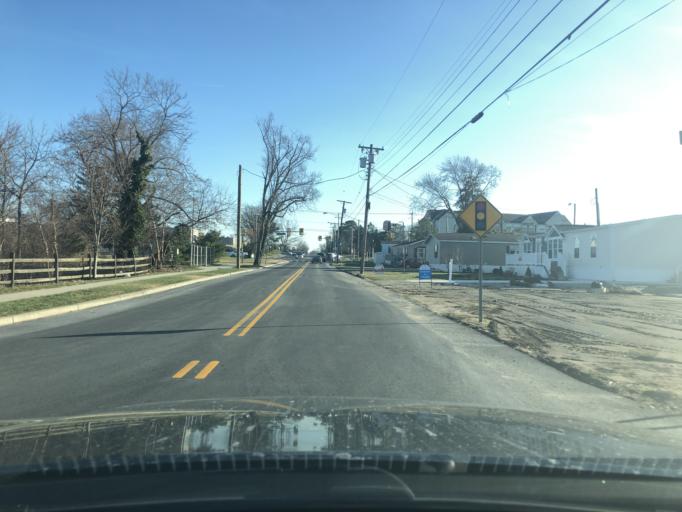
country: US
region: New Jersey
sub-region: Atlantic County
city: Northfield
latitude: 39.3982
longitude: -74.5565
